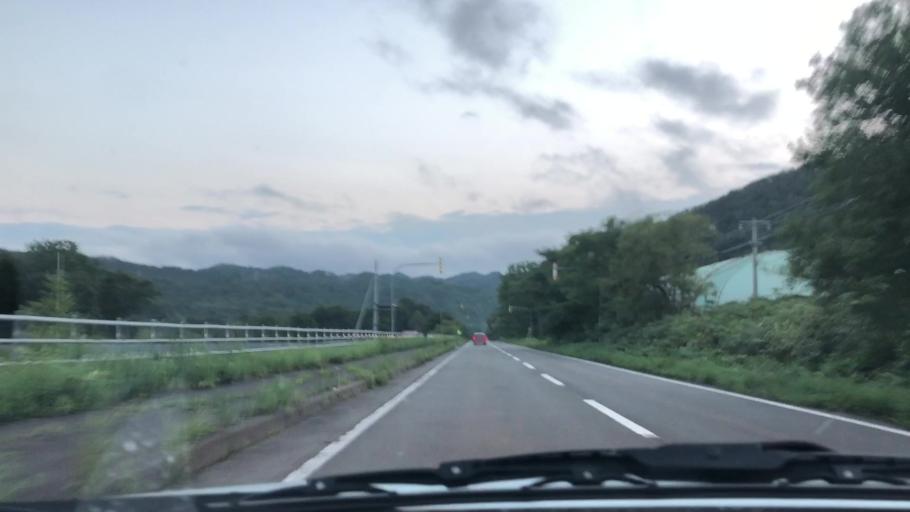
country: JP
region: Hokkaido
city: Chitose
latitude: 42.9117
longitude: 142.0201
